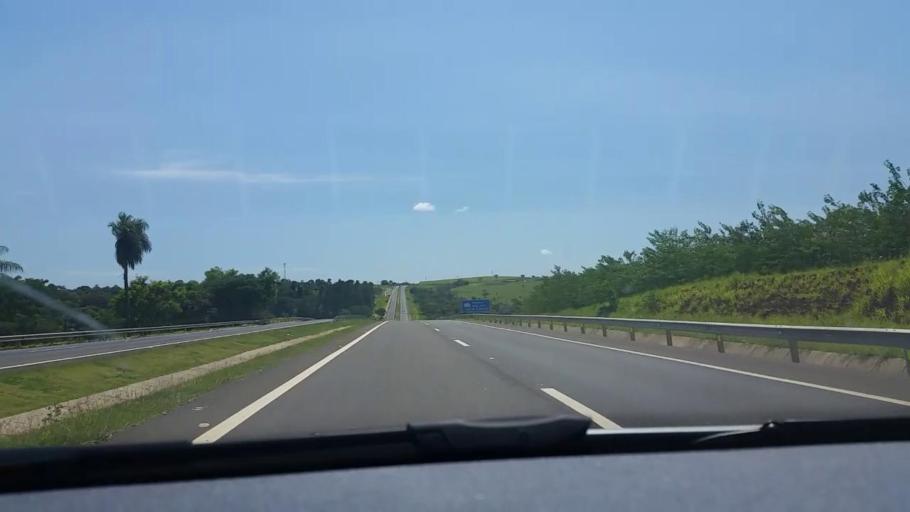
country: BR
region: Sao Paulo
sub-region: Bauru
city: Bauru
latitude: -22.4106
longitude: -49.1018
